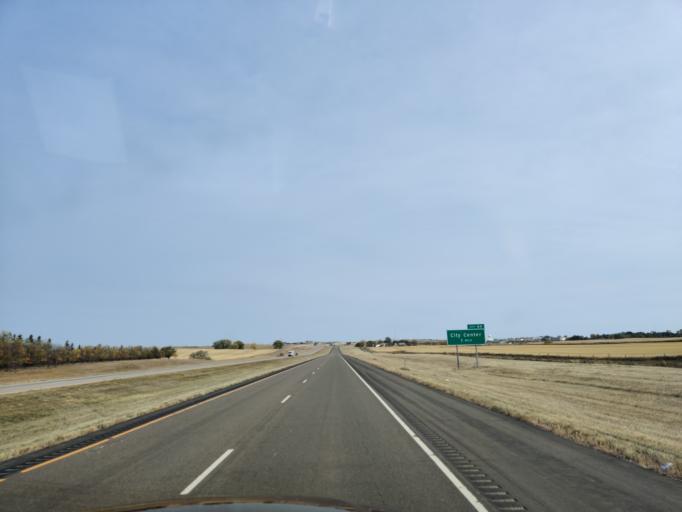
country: US
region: North Dakota
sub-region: Stark County
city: Dickinson
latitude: 46.8938
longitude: -102.7627
